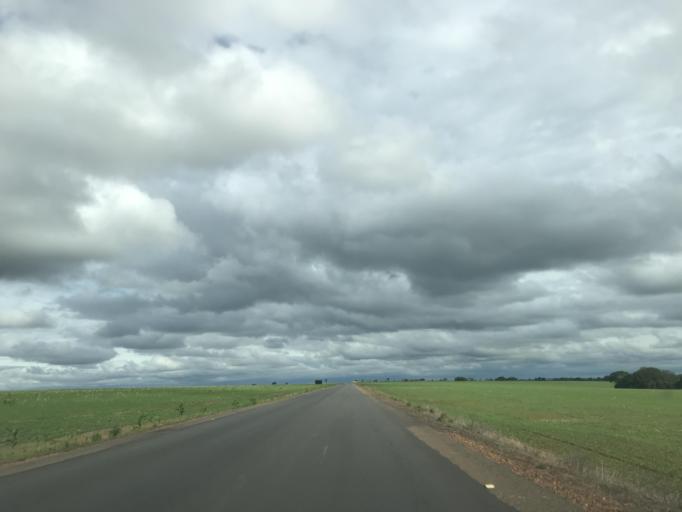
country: BR
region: Goias
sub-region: Vianopolis
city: Vianopolis
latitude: -16.9612
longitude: -48.6248
